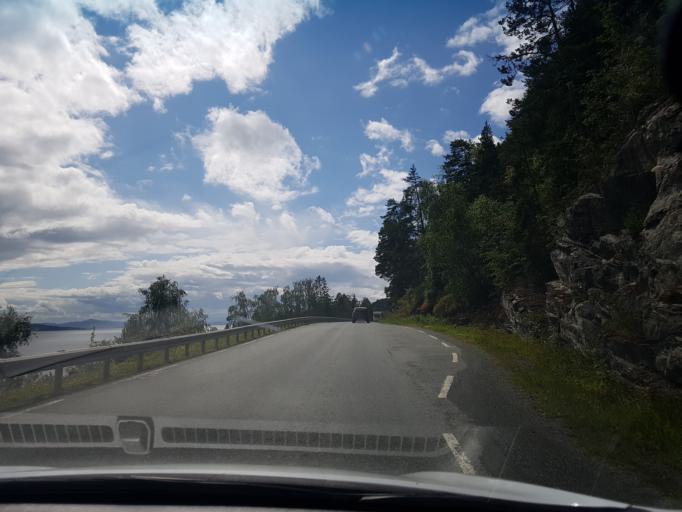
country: NO
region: Nord-Trondelag
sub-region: Frosta
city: Frosta
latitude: 63.6019
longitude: 10.8699
